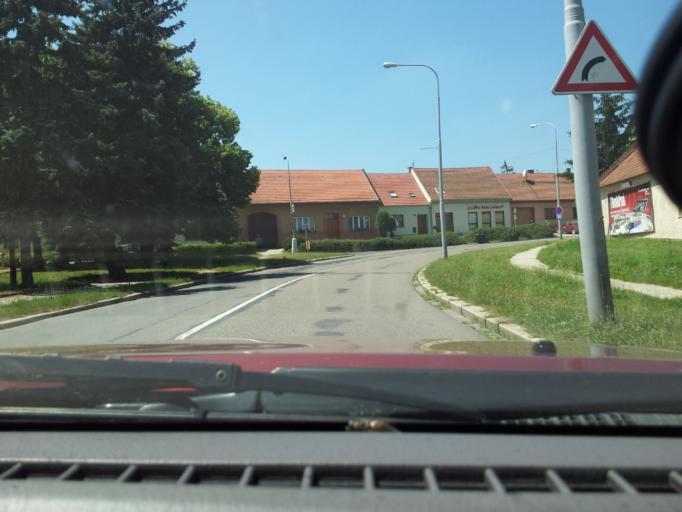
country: CZ
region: South Moravian
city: Modrice
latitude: 49.1525
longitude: 16.6547
